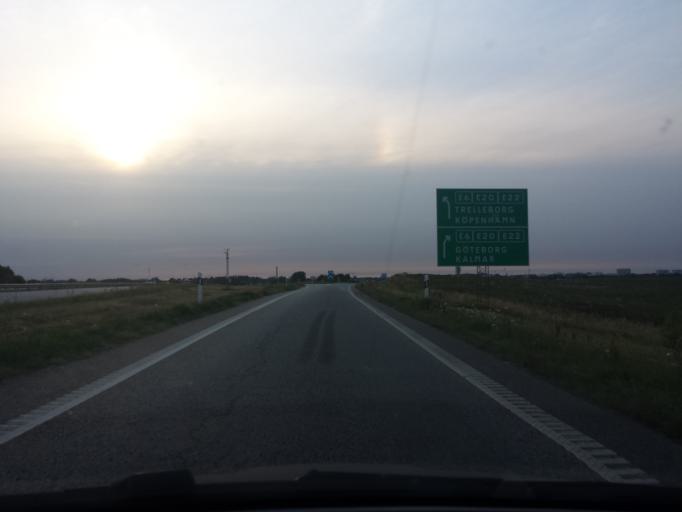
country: SE
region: Skane
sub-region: Malmo
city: Oxie
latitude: 55.5585
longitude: 13.0863
